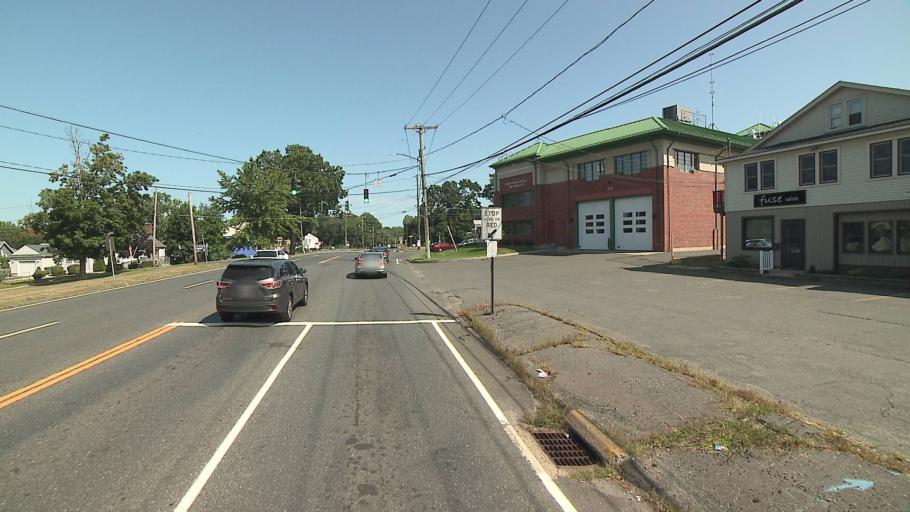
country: US
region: Connecticut
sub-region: Hartford County
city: Thompsonville
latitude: 42.0125
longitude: -72.5934
